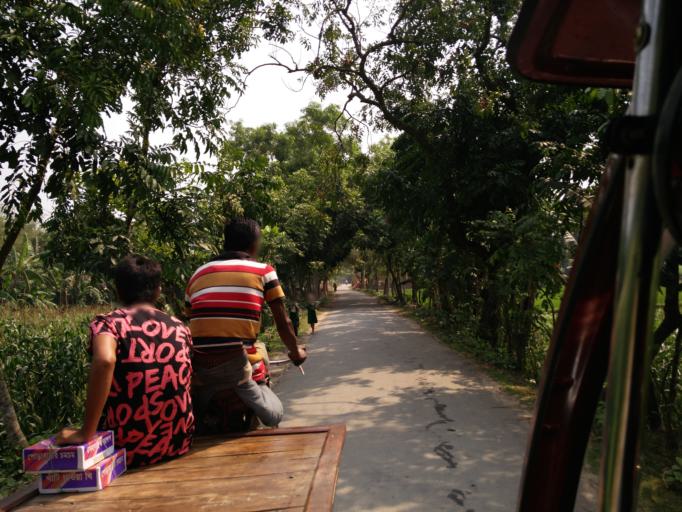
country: BD
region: Dhaka
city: Muktagacha
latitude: 24.9190
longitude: 90.2358
